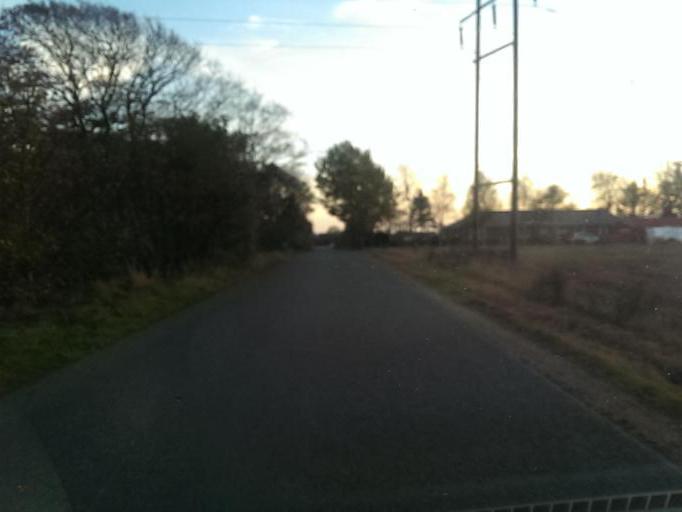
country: DK
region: South Denmark
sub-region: Esbjerg Kommune
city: Tjaereborg
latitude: 55.4728
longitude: 8.6155
